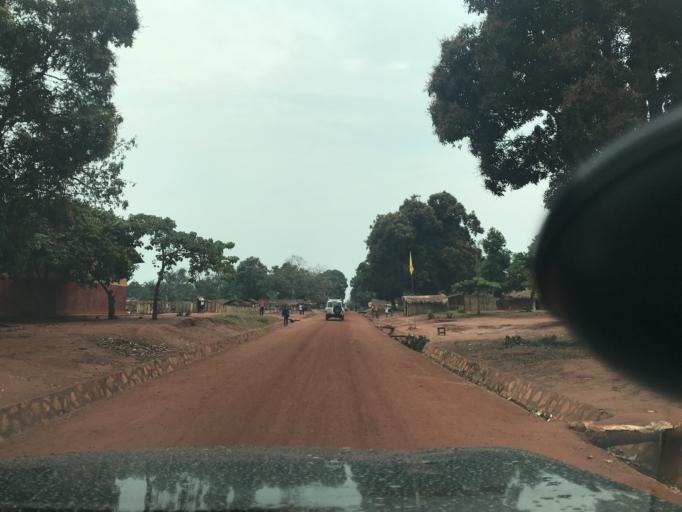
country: CD
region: Equateur
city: Gemena
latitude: 3.2210
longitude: 19.7790
